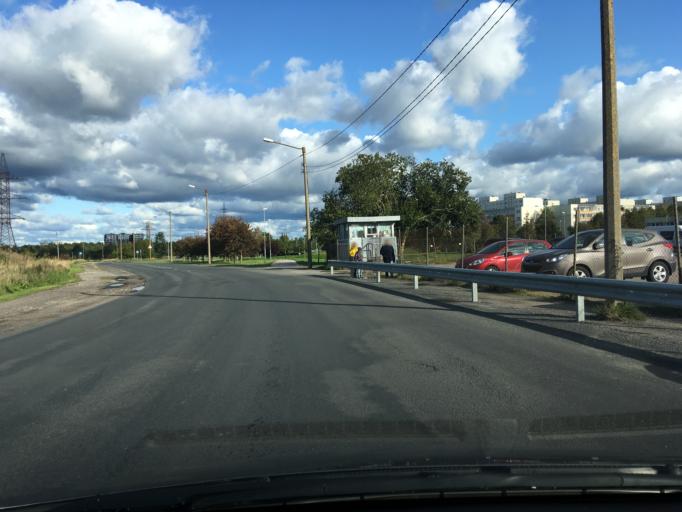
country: EE
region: Harju
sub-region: Tallinna linn
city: Kose
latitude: 59.4440
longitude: 24.8401
